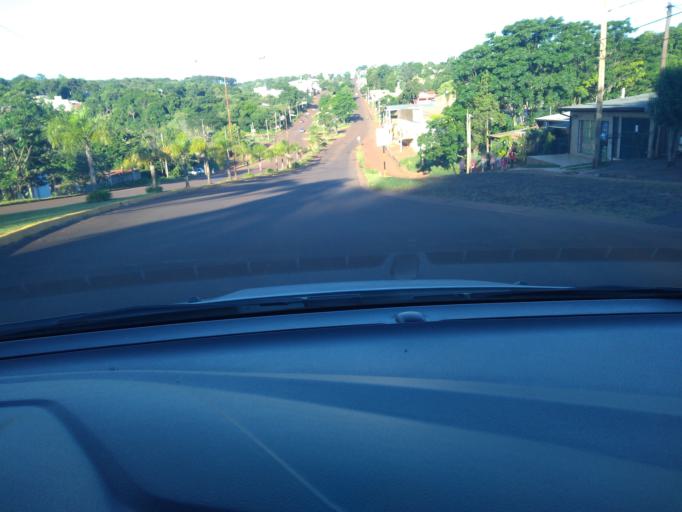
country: AR
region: Misiones
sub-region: Departamento de Obera
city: Obera
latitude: -27.4804
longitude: -55.1082
